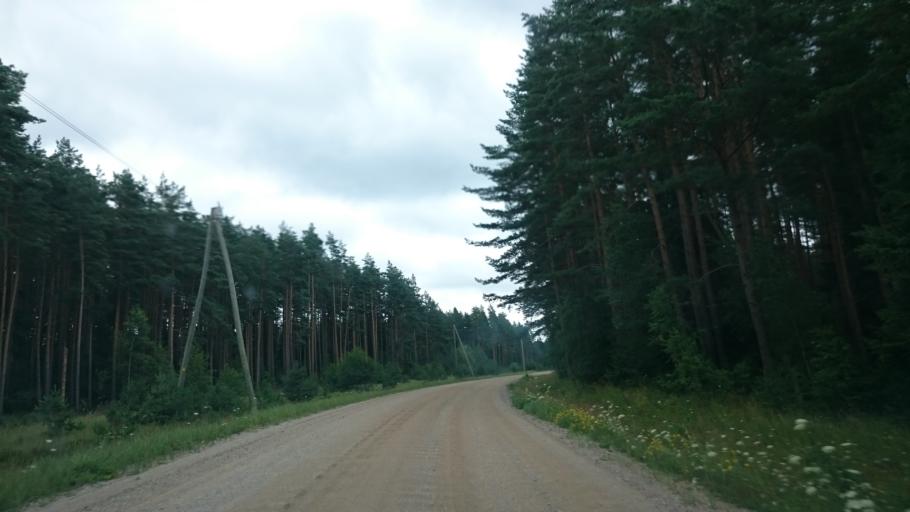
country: LV
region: Pavilostas
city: Pavilosta
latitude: 56.7682
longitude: 21.2958
